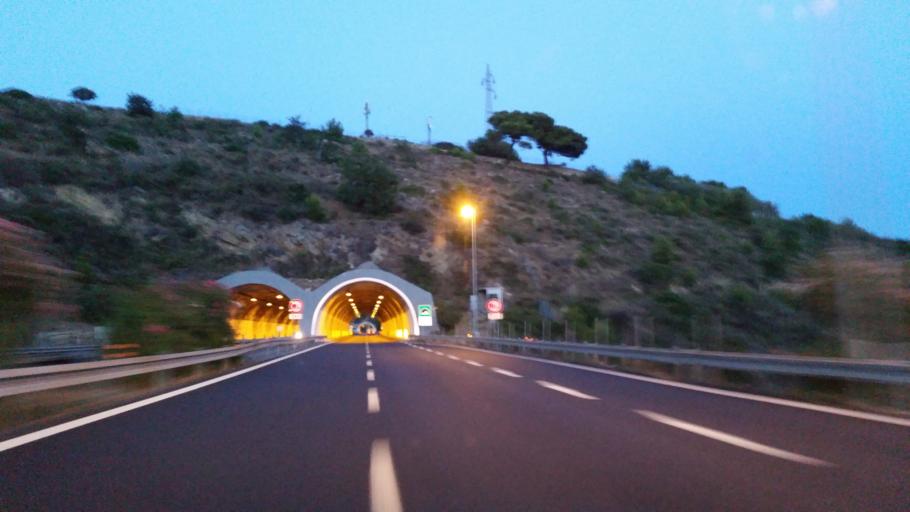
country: IT
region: Liguria
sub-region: Provincia di Imperia
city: Terzorio
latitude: 43.8513
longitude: 7.9106
